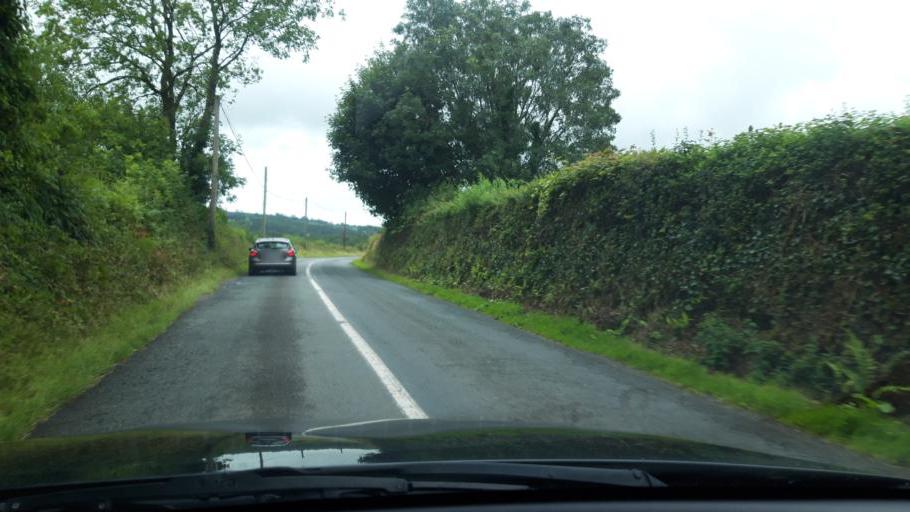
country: IE
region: Munster
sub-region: County Cork
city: Youghal
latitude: 52.1653
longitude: -7.8513
